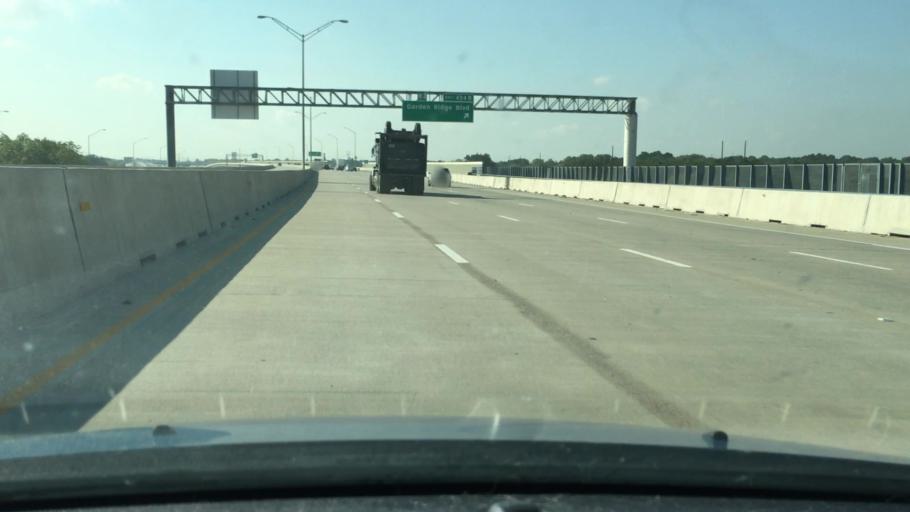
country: US
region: Texas
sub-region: Denton County
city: Highland Village
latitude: 33.0984
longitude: -97.0288
